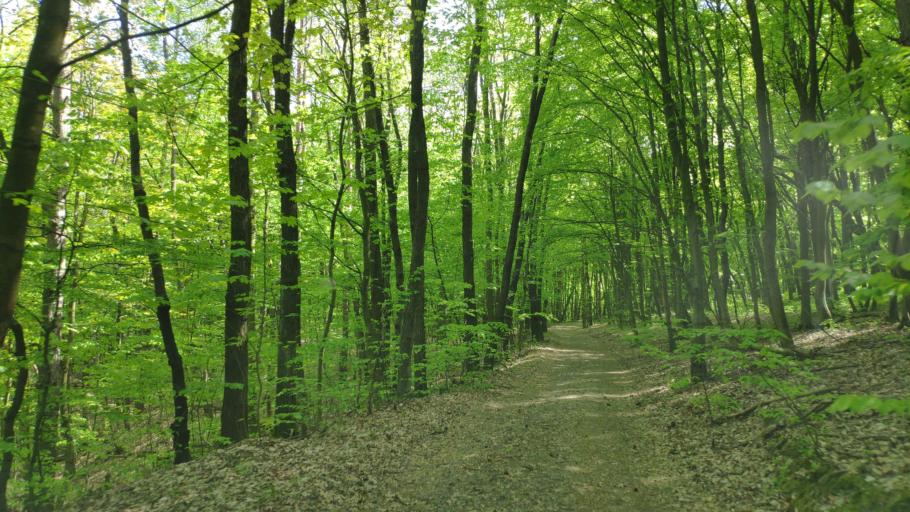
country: SK
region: Kosicky
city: Kosice
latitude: 48.6731
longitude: 21.4340
